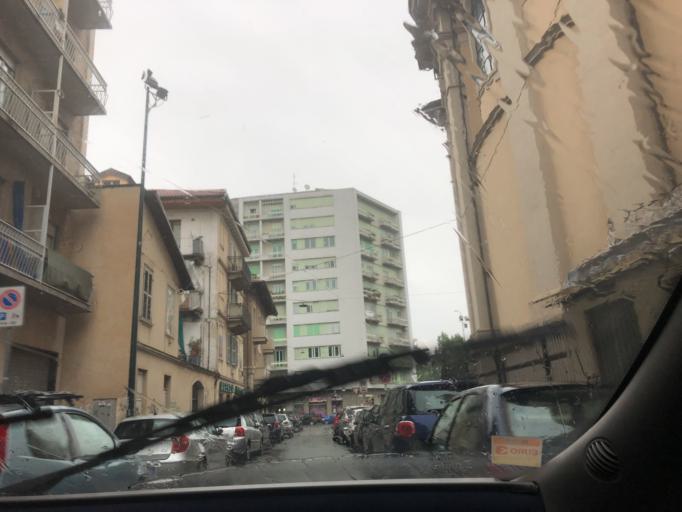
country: IT
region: Piedmont
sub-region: Provincia di Torino
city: Turin
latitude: 45.0809
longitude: 7.6549
